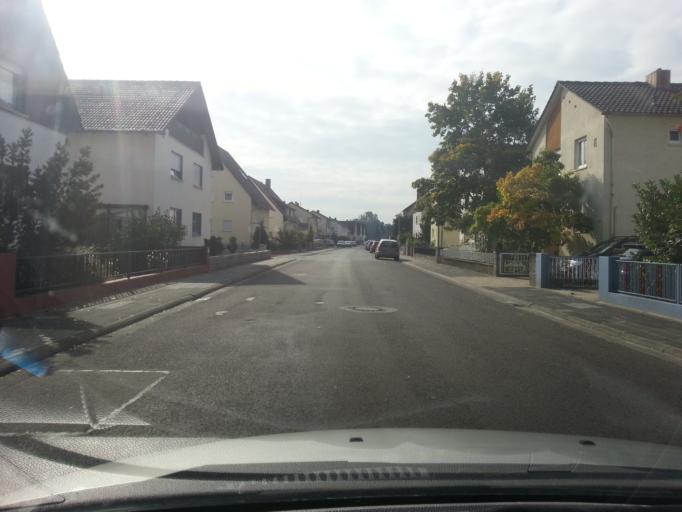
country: DE
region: Rheinland-Pfalz
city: Hassloch
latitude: 49.3522
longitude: 8.2557
